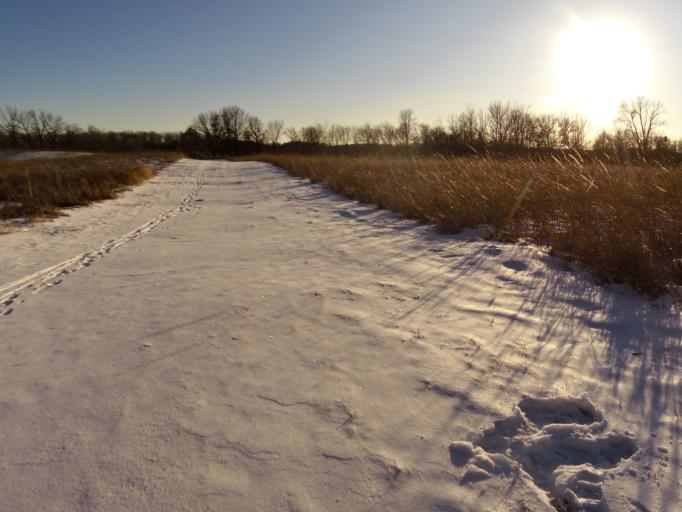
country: US
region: Minnesota
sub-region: Washington County
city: Lake Elmo
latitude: 44.9821
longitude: -92.9088
